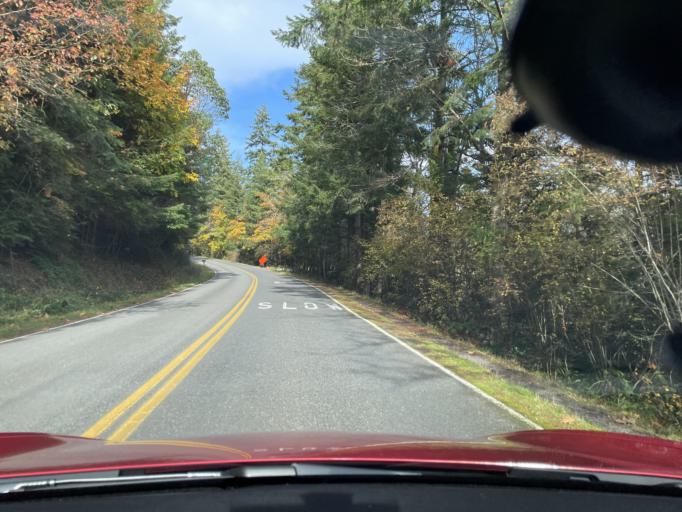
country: US
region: Washington
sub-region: San Juan County
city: Friday Harbor
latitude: 48.5302
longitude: -123.0050
